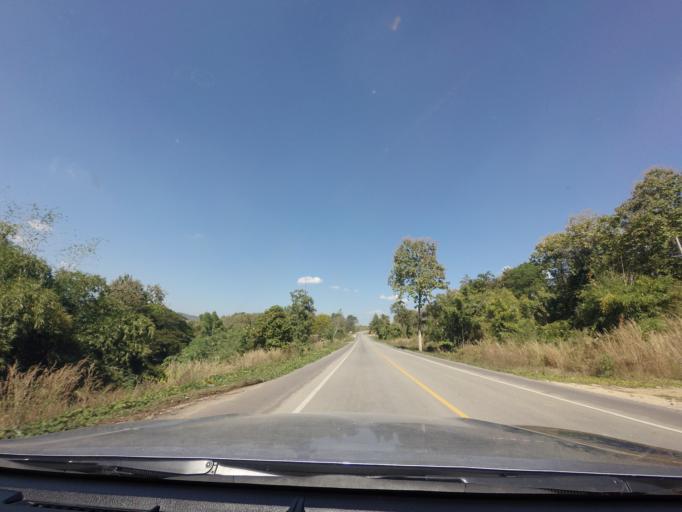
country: TH
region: Lampang
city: Mae Mo
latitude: 18.4788
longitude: 99.6351
